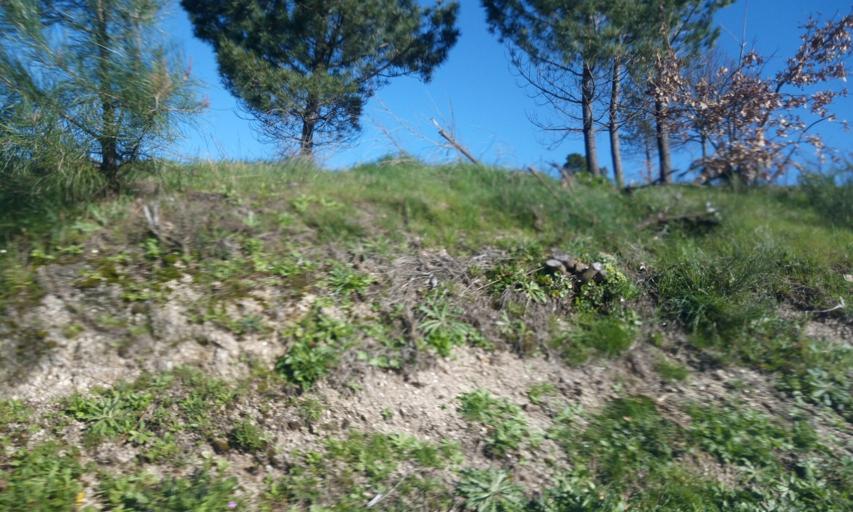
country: PT
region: Guarda
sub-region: Seia
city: Seia
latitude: 40.4697
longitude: -7.6224
